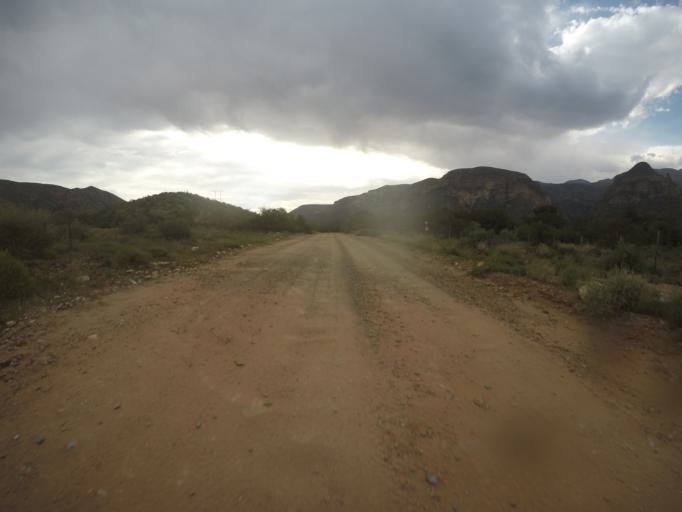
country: ZA
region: Eastern Cape
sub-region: Cacadu District Municipality
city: Willowmore
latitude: -33.5238
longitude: 23.8424
